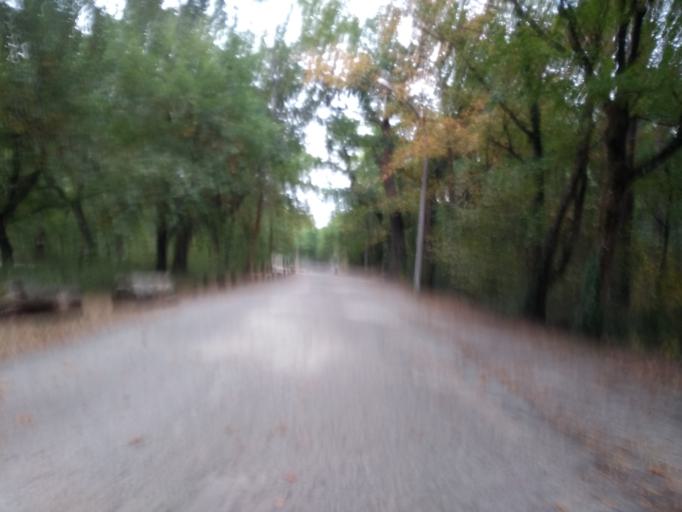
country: FR
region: Aquitaine
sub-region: Departement de la Gironde
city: Talence
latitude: 44.7913
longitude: -0.6005
